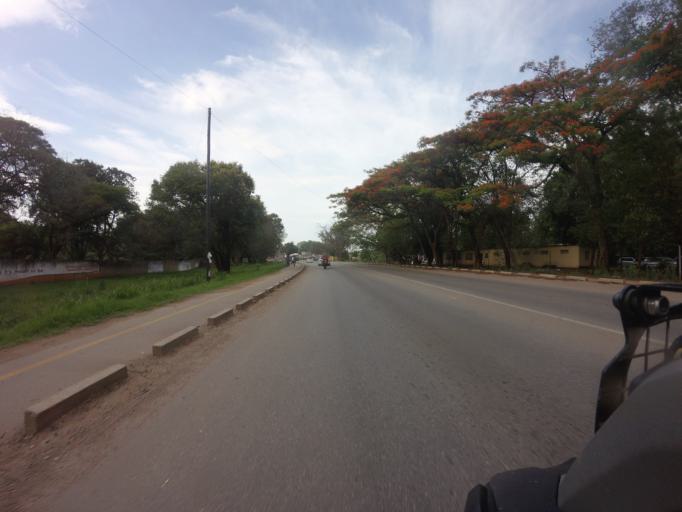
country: ZM
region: Lusaka
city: Lusaka
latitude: -15.5599
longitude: 28.2740
